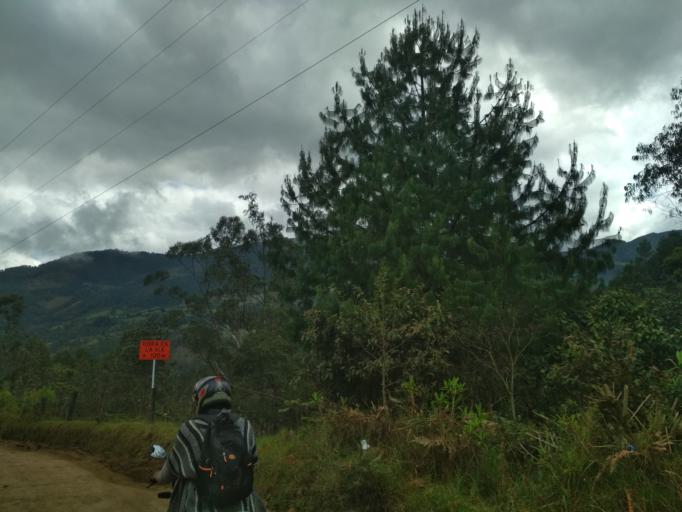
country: CO
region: Cauca
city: Jambalo
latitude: 2.7158
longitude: -76.3252
